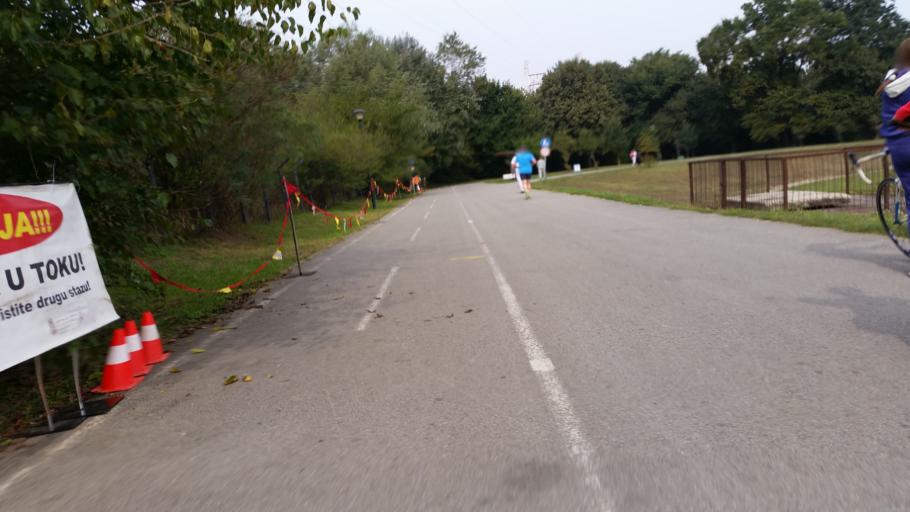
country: RS
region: Central Serbia
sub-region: Belgrade
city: Cukarica
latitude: 44.7774
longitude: 20.3731
